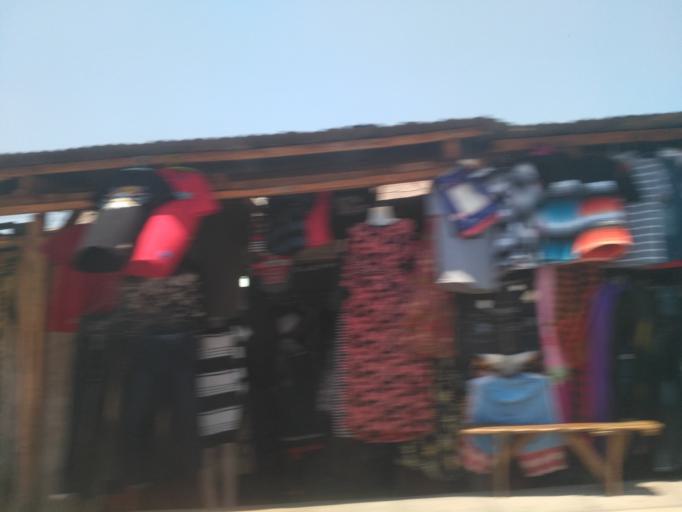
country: TZ
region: Dodoma
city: Dodoma
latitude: -6.1775
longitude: 35.7424
